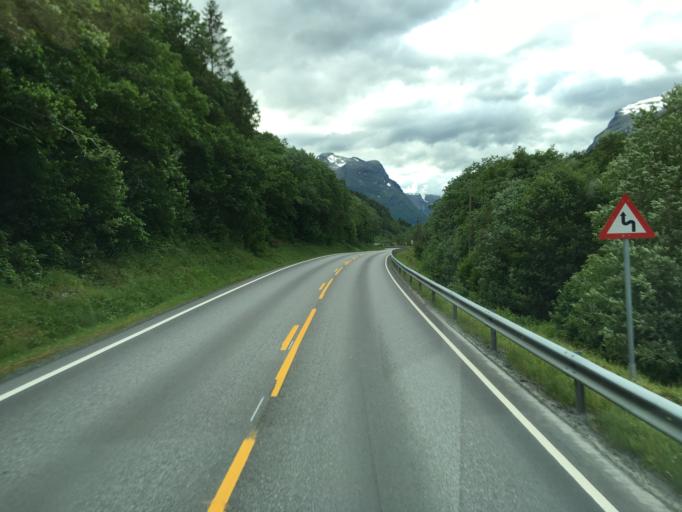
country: NO
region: More og Romsdal
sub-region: Sunndal
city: Sunndalsora
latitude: 62.6409
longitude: 8.7653
